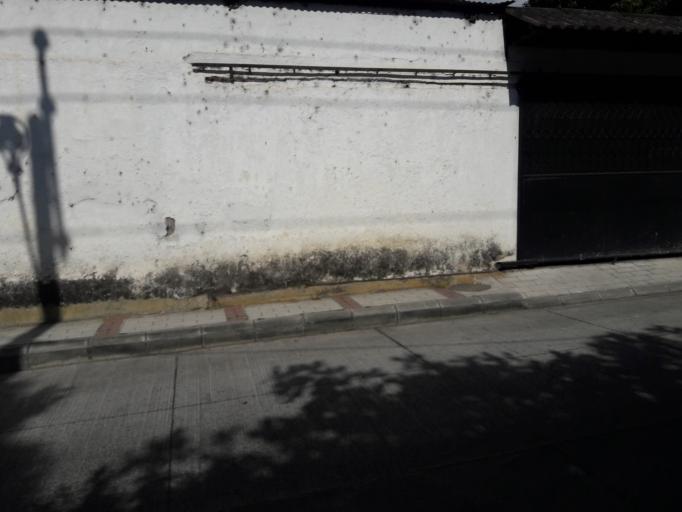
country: GT
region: Guatemala
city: Amatitlan
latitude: 14.4846
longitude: -90.6176
